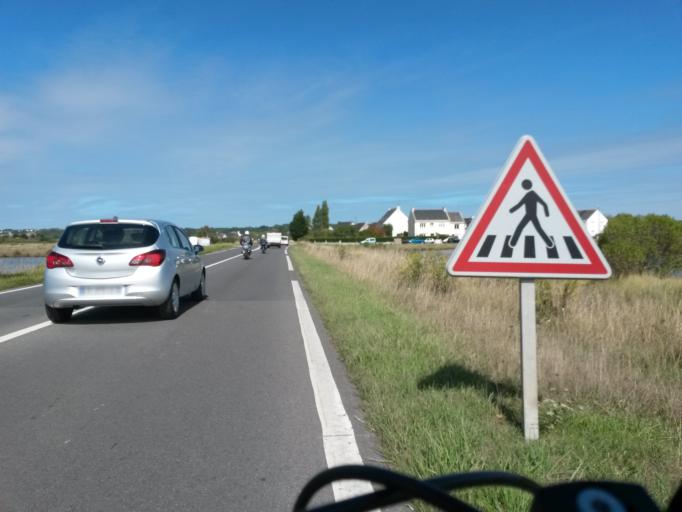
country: FR
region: Pays de la Loire
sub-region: Departement de la Loire-Atlantique
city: Le Pouliguen
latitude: 47.2978
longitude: -2.4342
